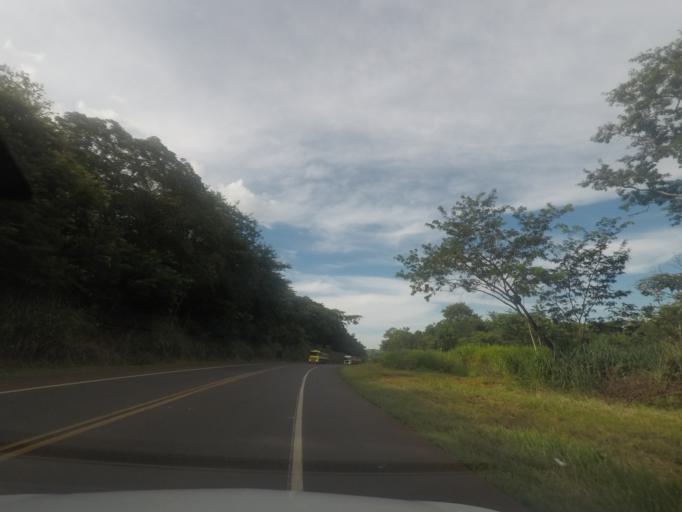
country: BR
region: Minas Gerais
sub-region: Monte Alegre De Minas
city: Monte Alegre de Minas
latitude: -19.0486
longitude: -49.0115
